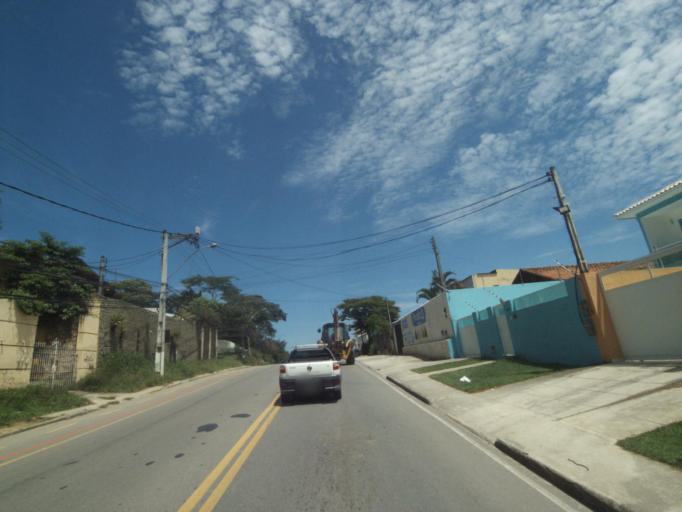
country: BR
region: Rio de Janeiro
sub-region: Niteroi
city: Niteroi
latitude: -22.9397
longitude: -43.0159
